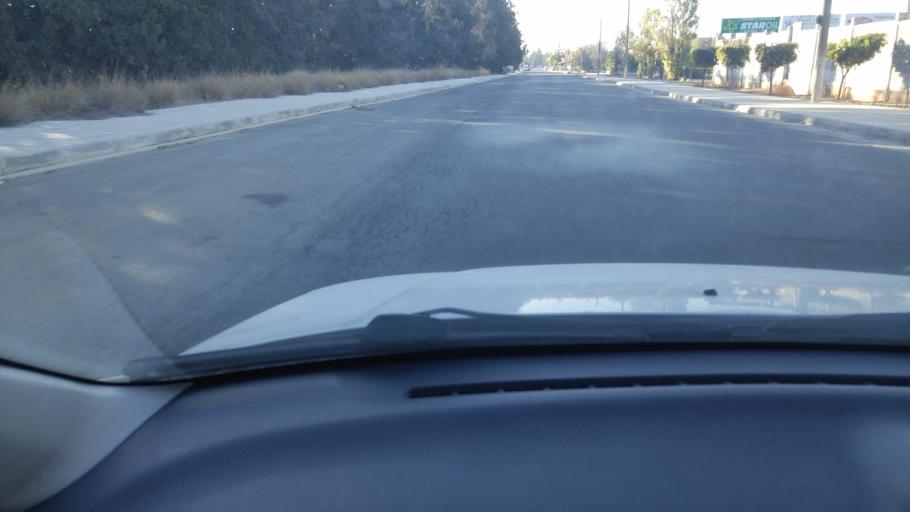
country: CY
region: Limassol
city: Ypsonas
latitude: 34.6594
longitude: 32.9719
